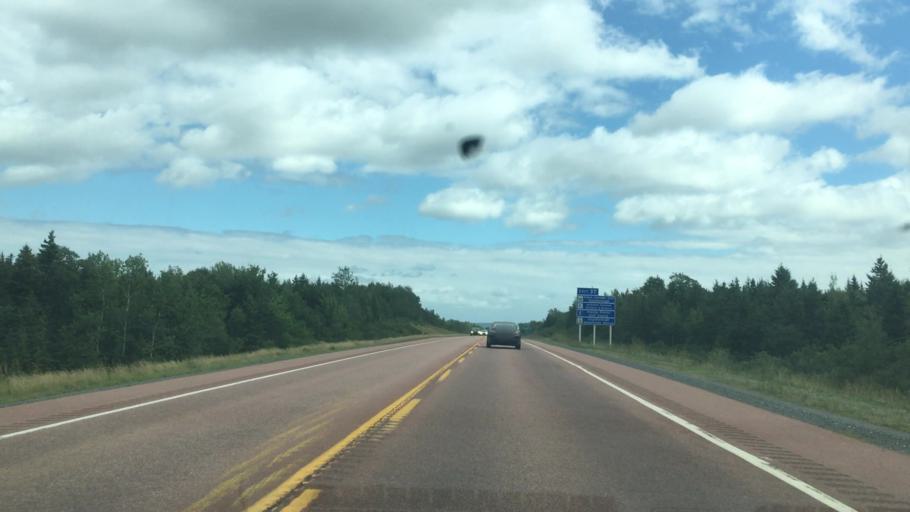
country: CA
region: Nova Scotia
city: Port Hawkesbury
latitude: 45.6069
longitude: -61.6691
